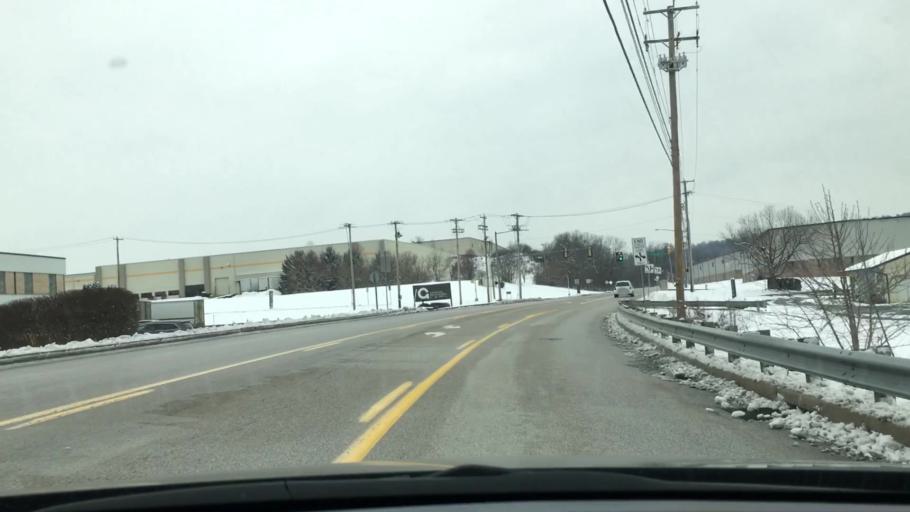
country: US
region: Pennsylvania
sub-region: York County
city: Emigsville
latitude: 40.0117
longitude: -76.7161
